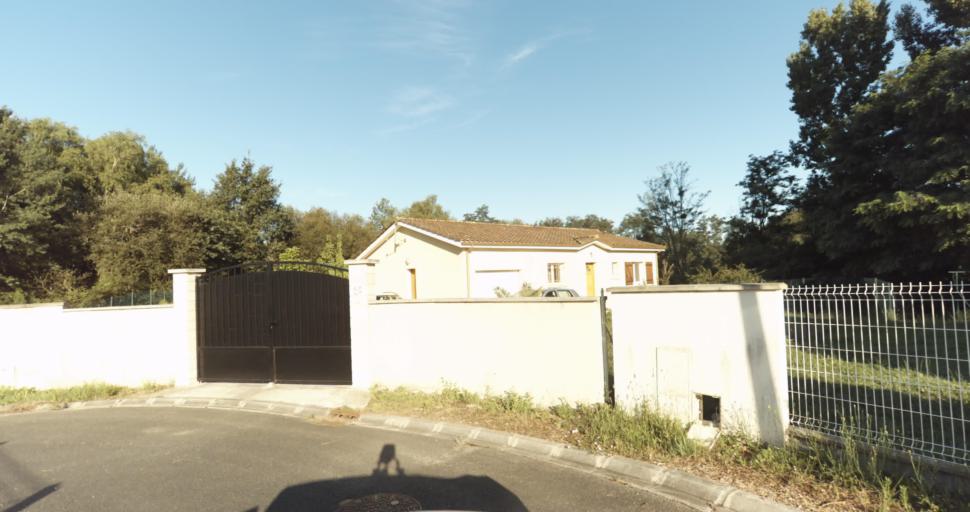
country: FR
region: Aquitaine
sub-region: Departement de la Gironde
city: Bazas
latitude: 44.4204
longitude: -0.2194
